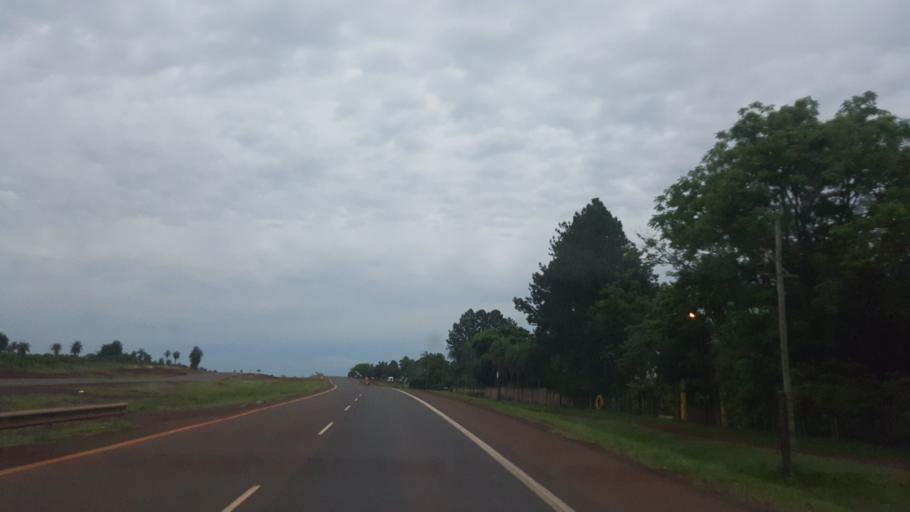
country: AR
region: Misiones
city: Garupa
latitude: -27.5389
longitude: -55.8537
